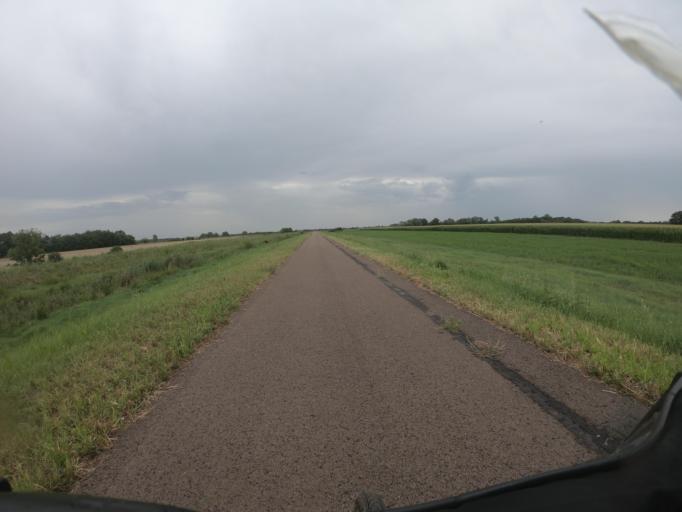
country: HU
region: Heves
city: Poroszlo
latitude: 47.7070
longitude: 20.6772
